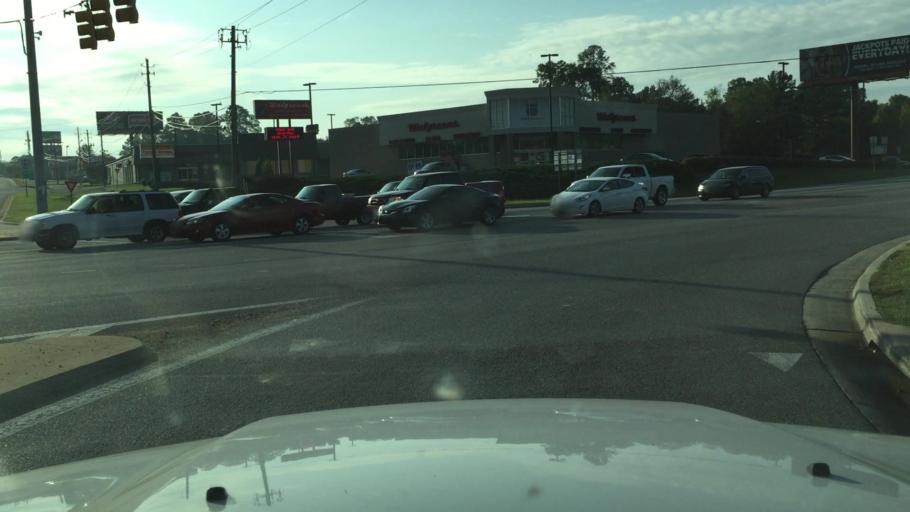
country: US
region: Alabama
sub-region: Tuscaloosa County
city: Northport
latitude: 33.2388
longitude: -87.5768
